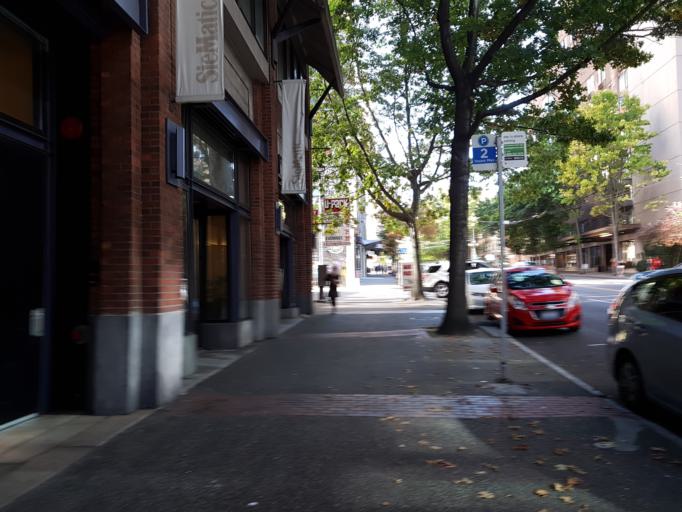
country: US
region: Washington
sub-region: King County
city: Seattle
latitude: 47.6119
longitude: -122.3435
